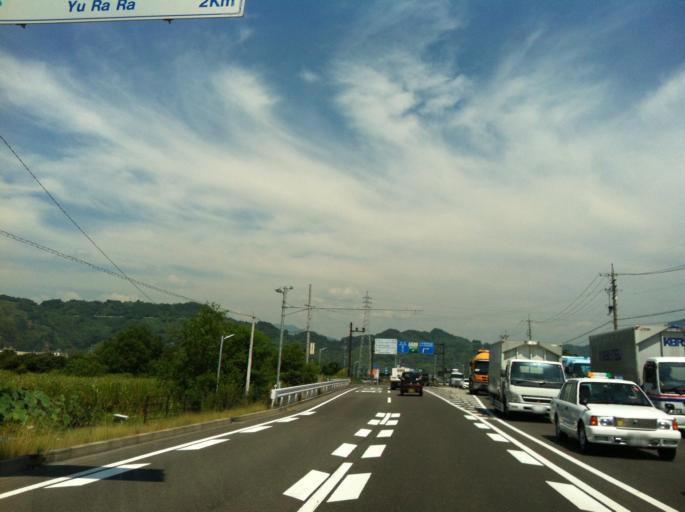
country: JP
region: Shizuoka
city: Shizuoka-shi
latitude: 35.0106
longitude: 138.4005
